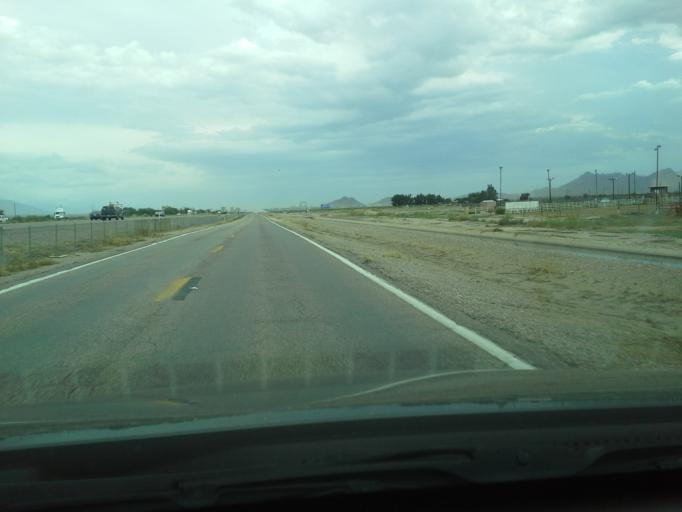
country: US
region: Arizona
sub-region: Pima County
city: Marana
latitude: 32.4525
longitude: -111.2034
